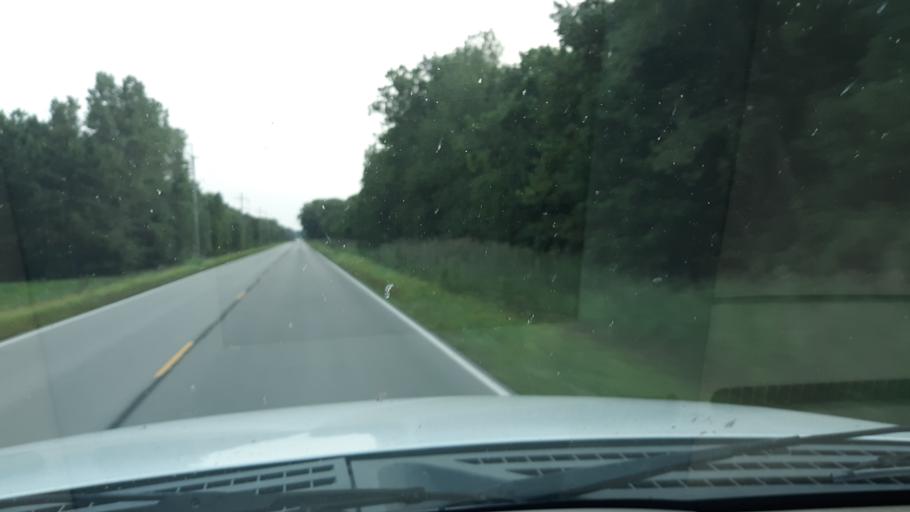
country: US
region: Illinois
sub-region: White County
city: Norris City
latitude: 37.9471
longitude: -88.3405
